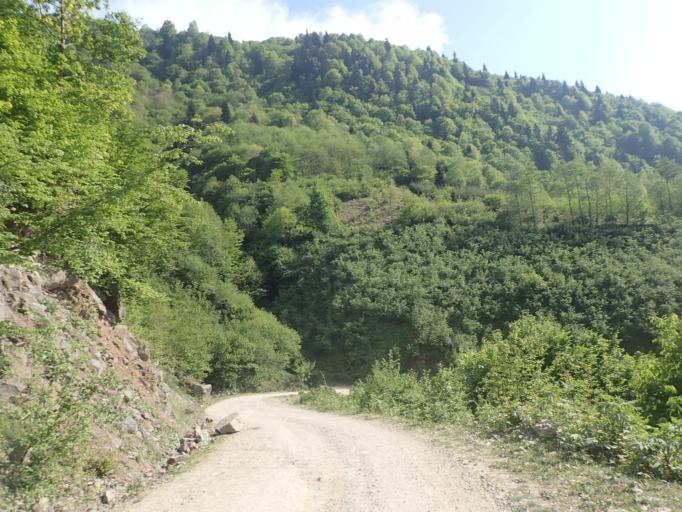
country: TR
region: Ordu
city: Topcam
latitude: 40.7045
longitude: 37.8579
